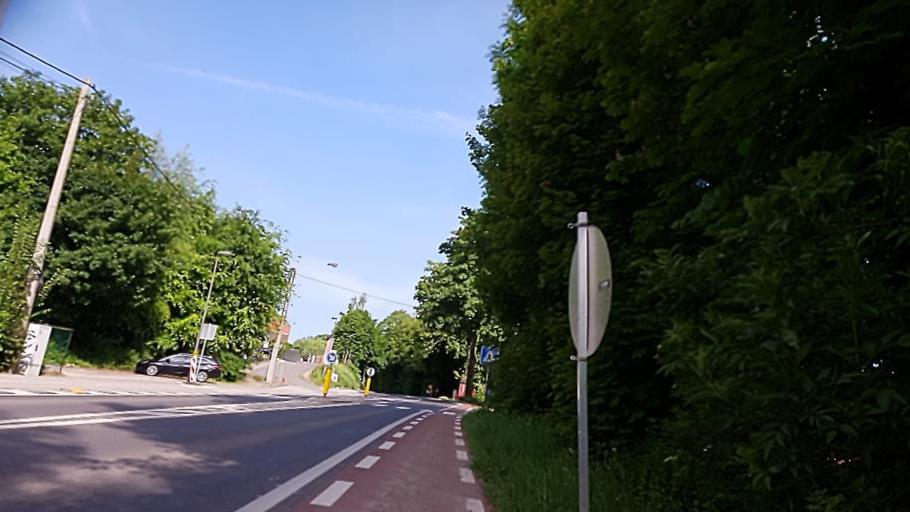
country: BE
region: Wallonia
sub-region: Province du Brabant Wallon
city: Wavre
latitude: 50.7242
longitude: 4.6028
